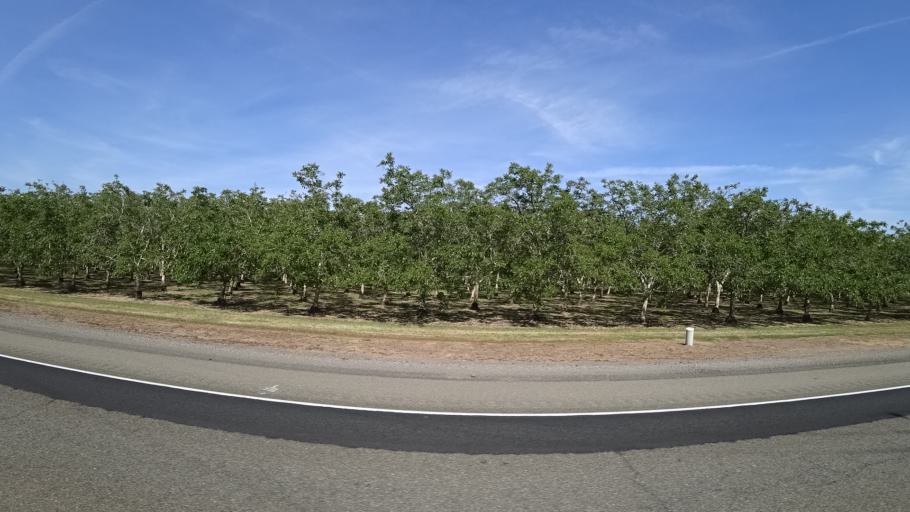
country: US
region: California
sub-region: Tehama County
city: Los Molinos
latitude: 39.9798
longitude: -122.0788
